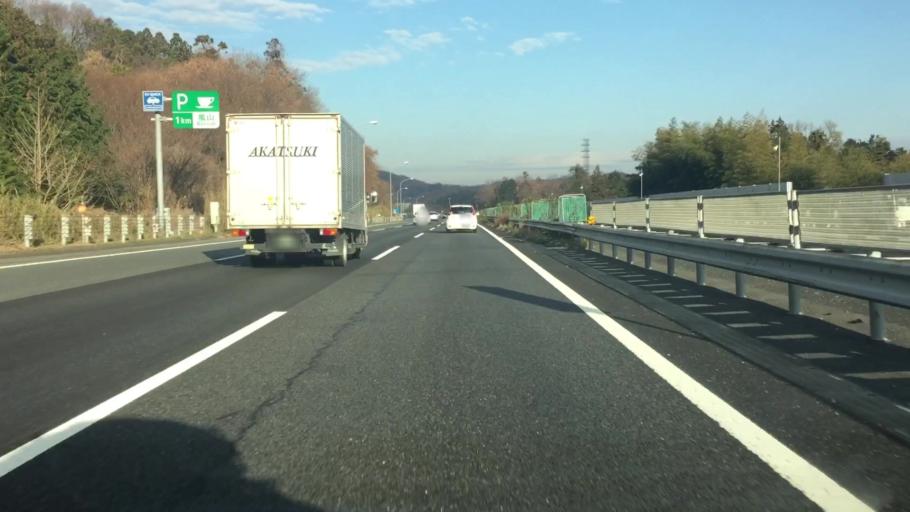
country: JP
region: Saitama
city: Ogawa
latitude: 36.0779
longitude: 139.3003
